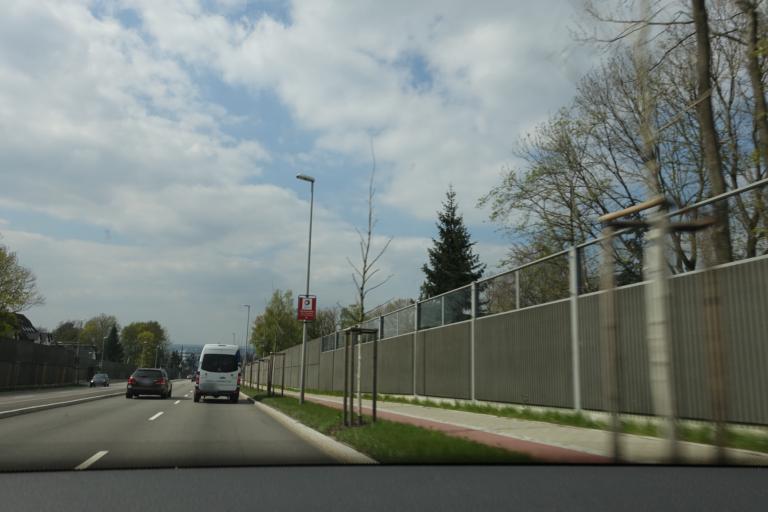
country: DE
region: Saxony
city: Hilbersdorf
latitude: 50.8085
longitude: 12.9681
